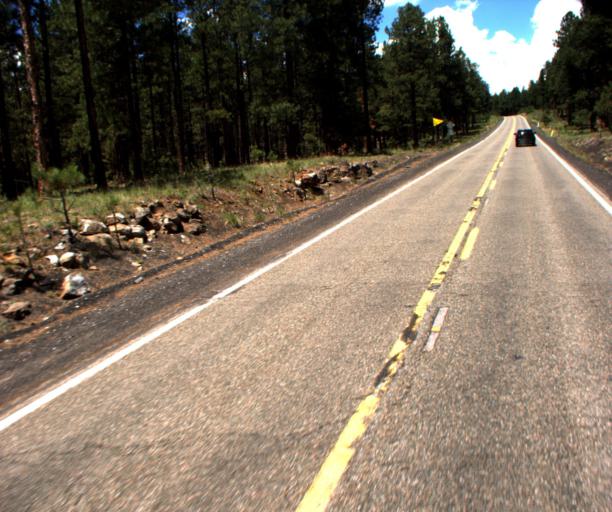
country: US
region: Arizona
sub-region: Coconino County
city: Flagstaff
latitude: 35.3005
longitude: -111.7665
